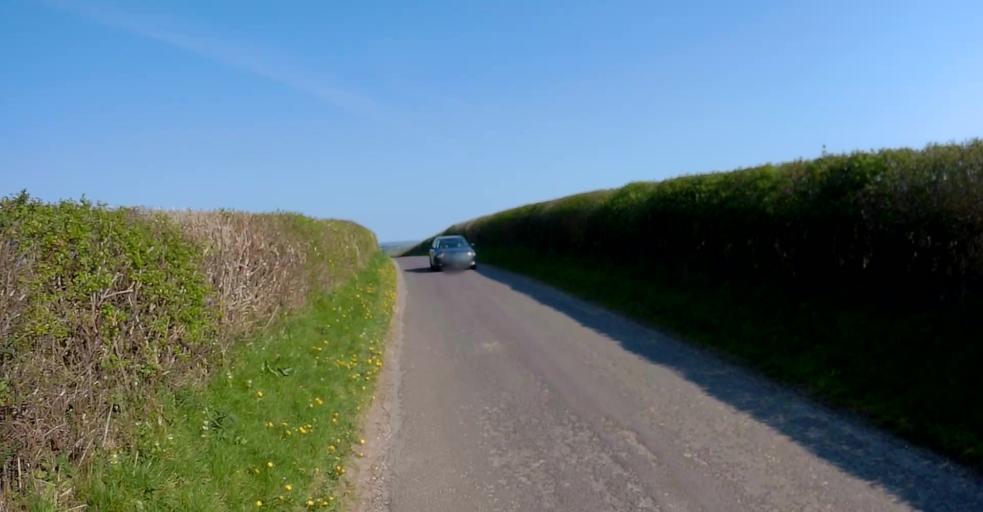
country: GB
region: England
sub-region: Hampshire
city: Kings Worthy
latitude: 51.0963
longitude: -1.1769
